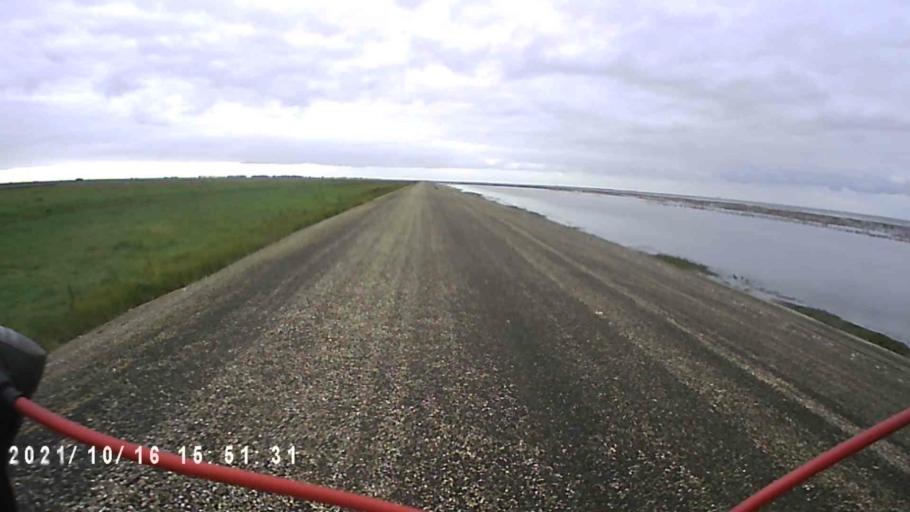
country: NL
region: Friesland
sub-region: Gemeente Dongeradeel
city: Anjum
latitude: 53.4046
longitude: 6.1321
